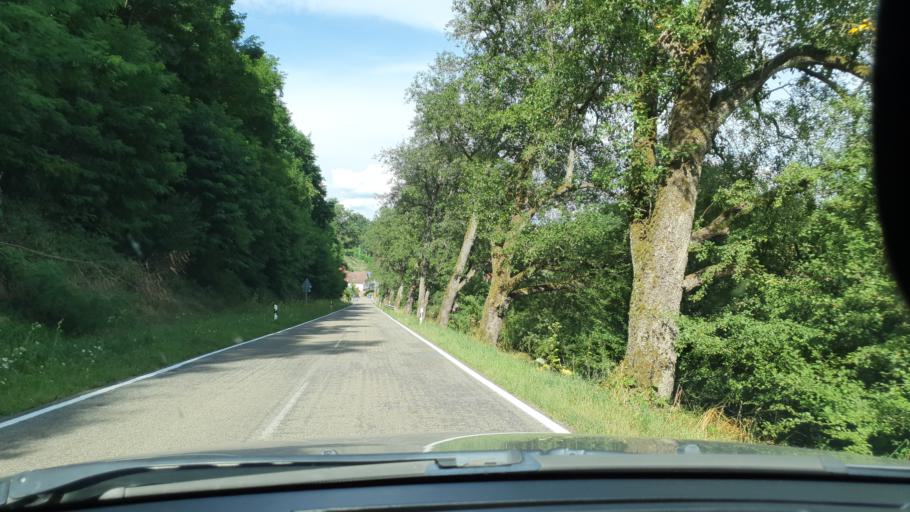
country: DE
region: Rheinland-Pfalz
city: Contwig
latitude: 49.2403
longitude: 7.4180
